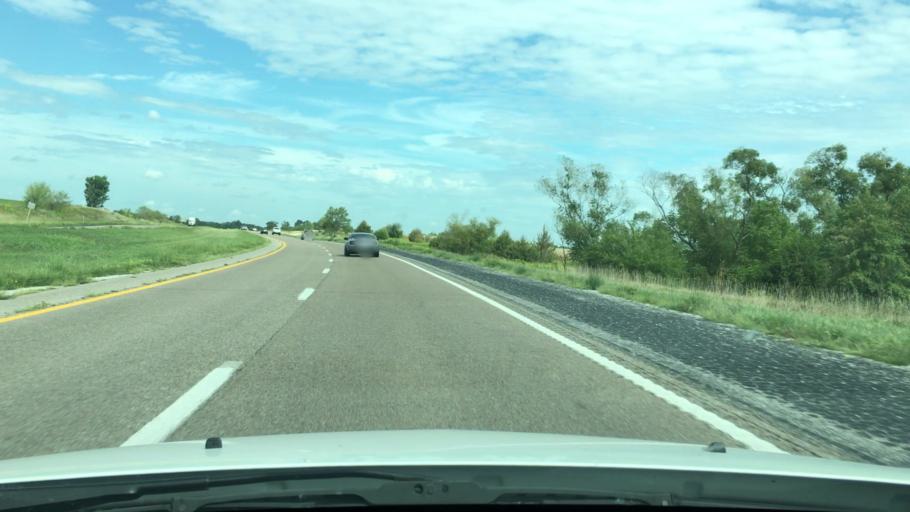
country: US
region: Missouri
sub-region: Audrain County
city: Mexico
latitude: 39.0299
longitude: -91.8860
